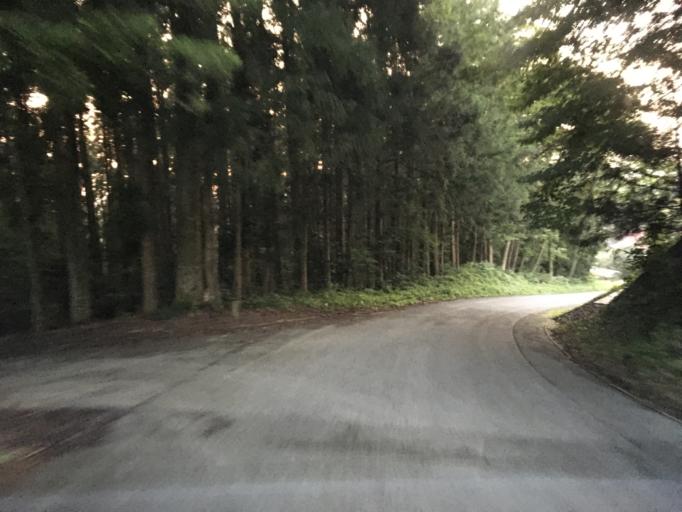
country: JP
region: Iwate
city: Ichinoseki
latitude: 38.8435
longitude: 141.2853
